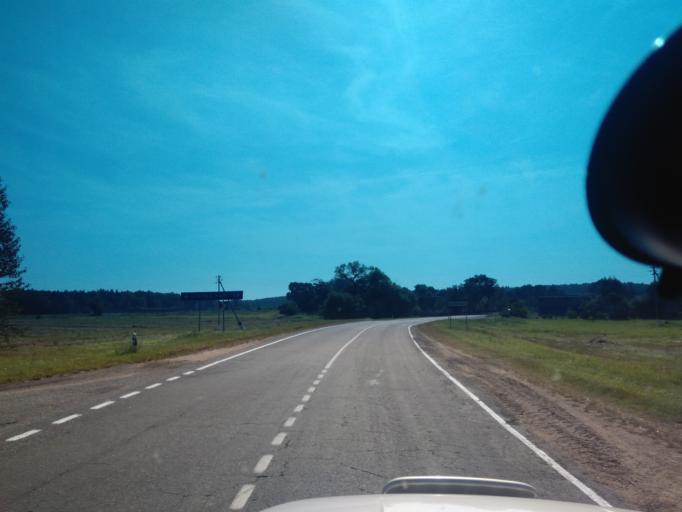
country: BY
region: Minsk
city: Uzda
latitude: 53.3905
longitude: 27.2417
